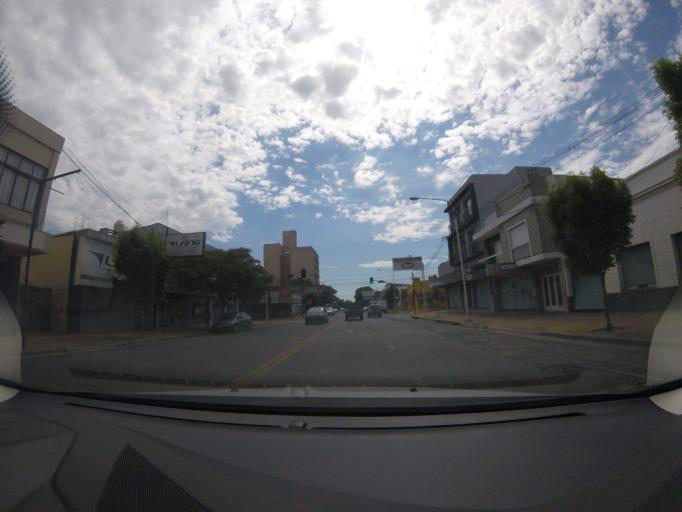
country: AR
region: Buenos Aires
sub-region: Partido de Tandil
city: Tandil
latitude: -37.3212
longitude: -59.1349
